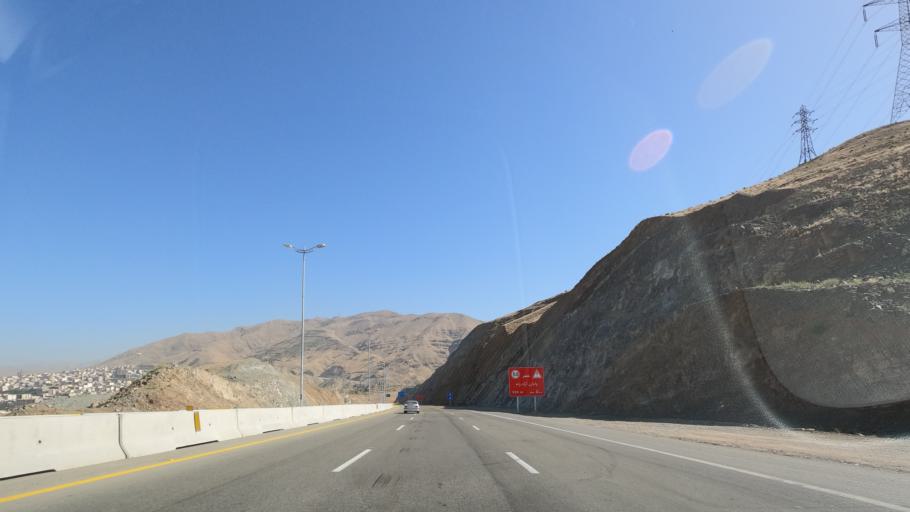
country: IR
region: Alborz
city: Karaj
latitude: 35.8162
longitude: 51.0378
